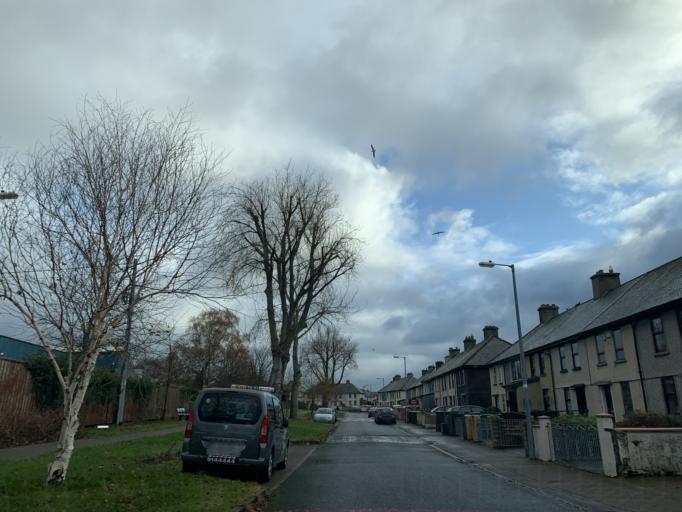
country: IE
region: Connaught
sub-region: Sligo
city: Sligo
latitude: 54.2694
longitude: -8.4640
